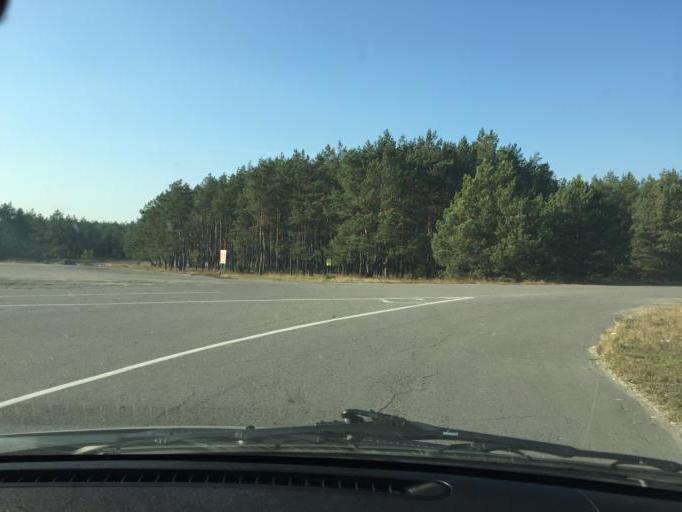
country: BY
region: Brest
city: Davyd-Haradok
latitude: 52.2356
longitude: 27.2431
